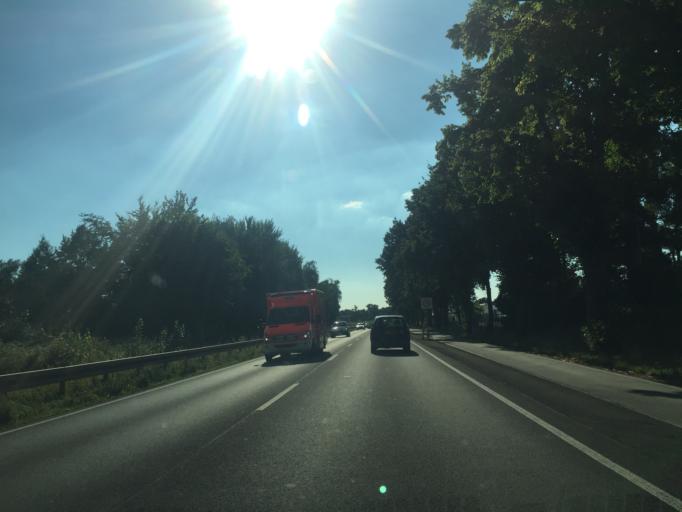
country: DE
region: North Rhine-Westphalia
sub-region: Regierungsbezirk Munster
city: Telgte
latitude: 51.9780
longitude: 7.7144
